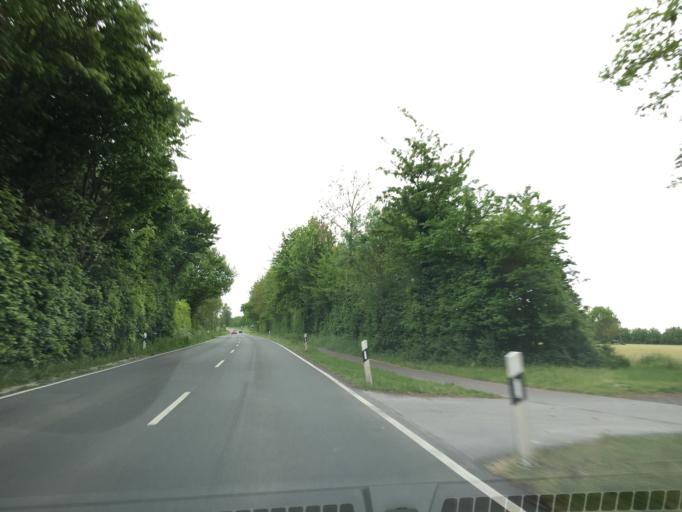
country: DE
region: North Rhine-Westphalia
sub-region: Regierungsbezirk Munster
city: Havixbeck
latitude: 51.9323
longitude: 7.4519
